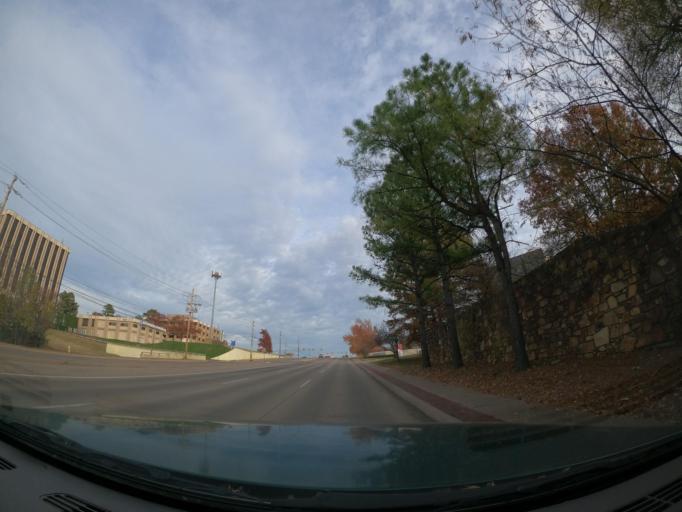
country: US
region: Oklahoma
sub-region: Tulsa County
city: Jenks
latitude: 36.0608
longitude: -95.9245
